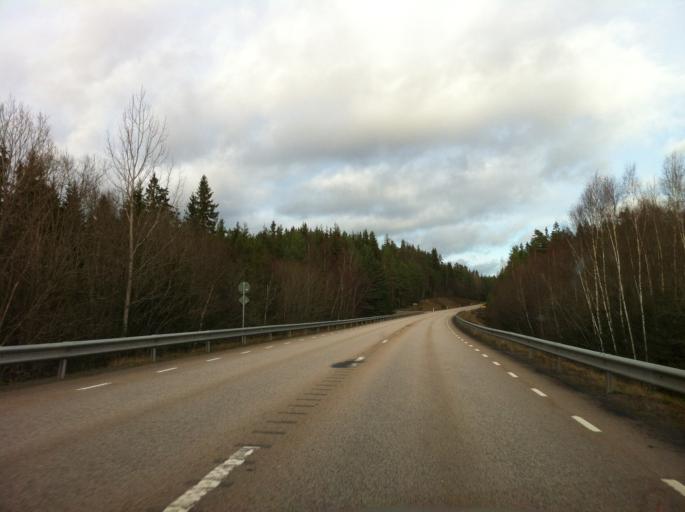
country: SE
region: Kronoberg
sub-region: Uppvidinge Kommun
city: Lenhovda
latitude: 57.0914
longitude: 15.1924
